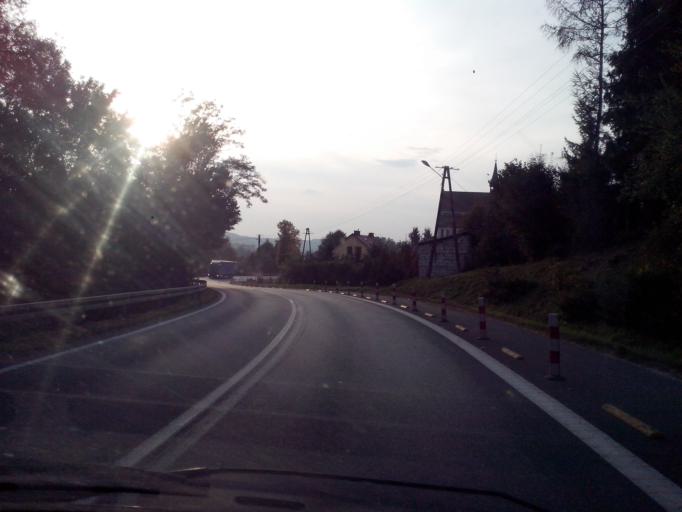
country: PL
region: Subcarpathian Voivodeship
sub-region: Powiat strzyzowski
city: Jawornik
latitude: 49.8049
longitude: 21.9045
